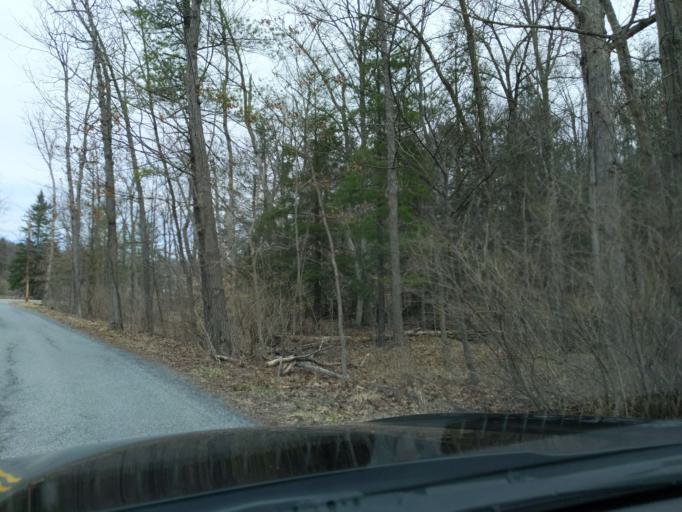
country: US
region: Pennsylvania
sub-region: Blair County
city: Greenwood
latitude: 40.5804
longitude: -78.3802
